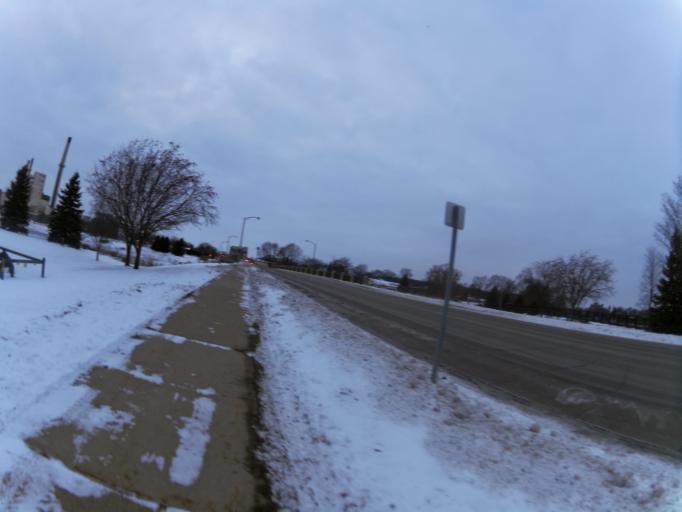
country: US
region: Minnesota
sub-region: Olmsted County
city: Rochester
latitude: 44.0303
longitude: -92.4570
